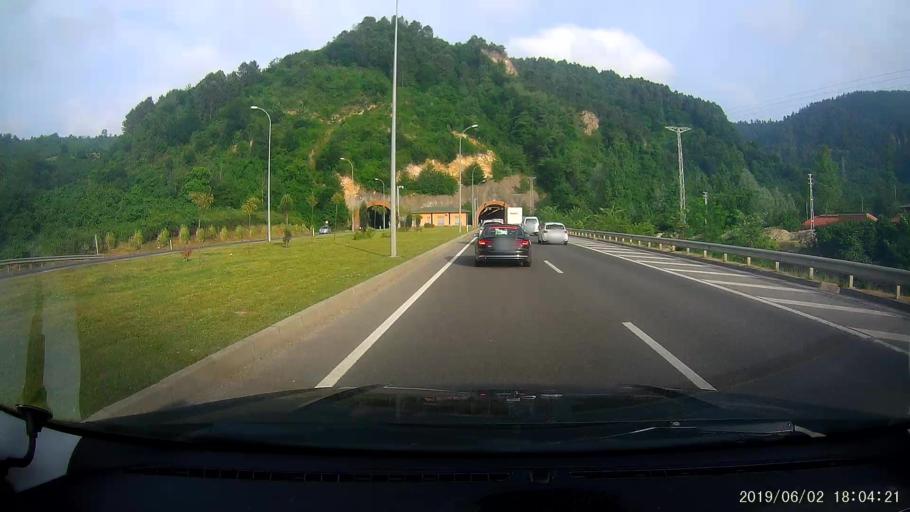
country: TR
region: Ordu
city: Unieh
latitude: 41.1209
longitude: 37.2296
